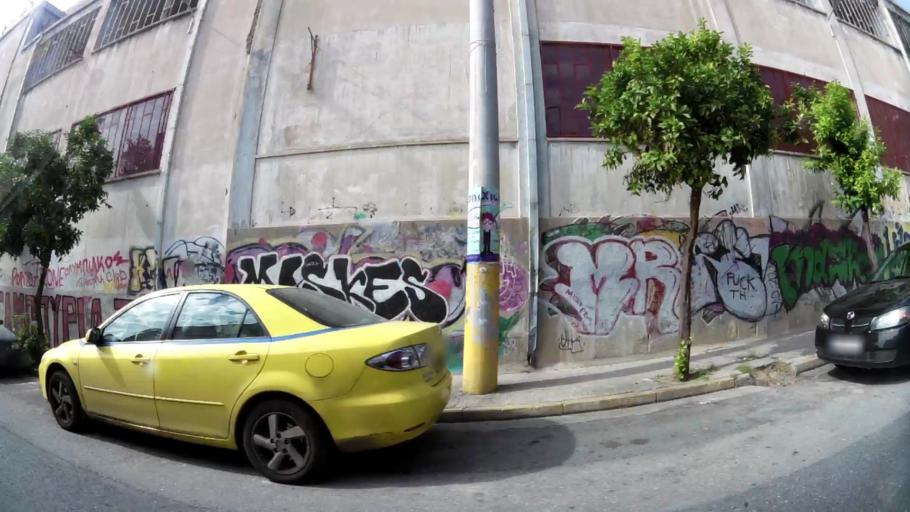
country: GR
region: Attica
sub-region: Nomos Piraios
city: Keratsini
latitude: 37.9623
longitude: 23.6255
